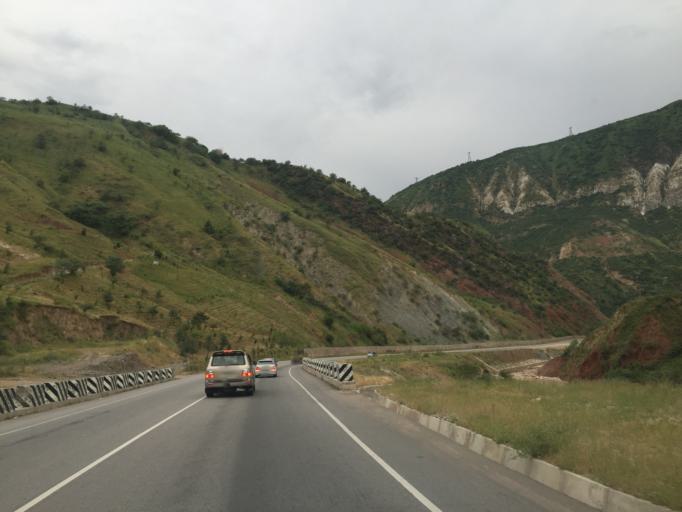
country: TJ
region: Khatlon
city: Norak
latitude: 38.4353
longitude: 69.2077
